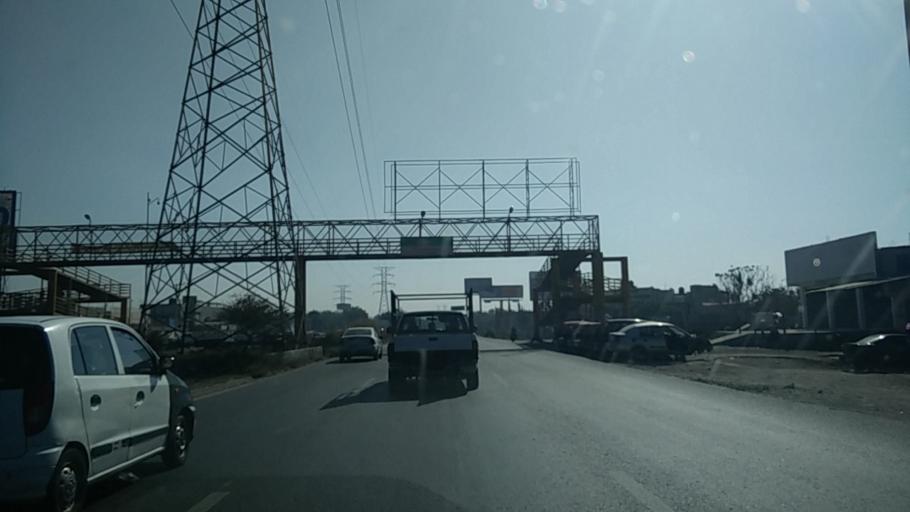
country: MX
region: Mexico
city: Santo Tomas Chiconautla
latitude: 19.6135
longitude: -99.0117
